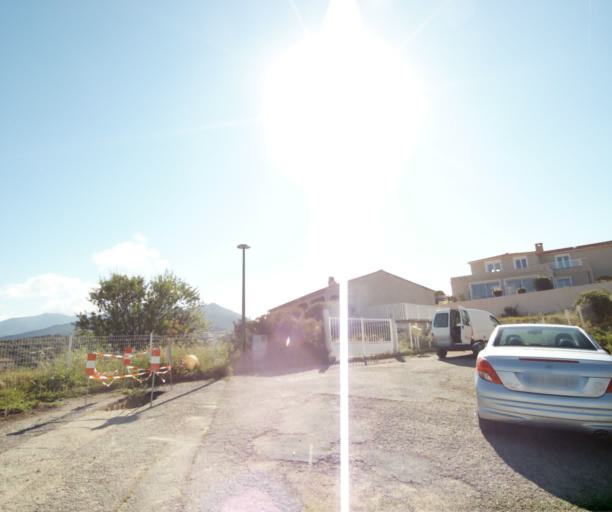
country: FR
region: Corsica
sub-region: Departement de la Corse-du-Sud
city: Propriano
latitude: 41.6713
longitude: 8.9025
